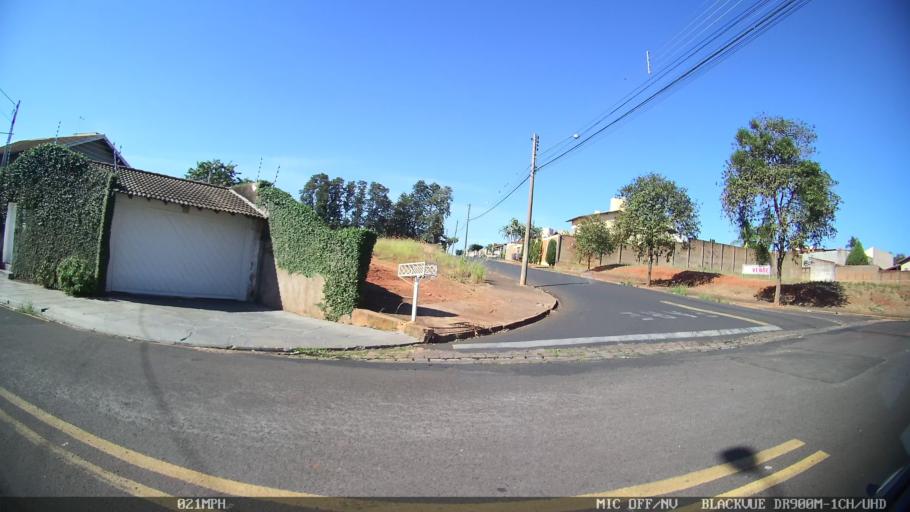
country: BR
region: Sao Paulo
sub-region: Olimpia
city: Olimpia
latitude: -20.7331
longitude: -48.9188
